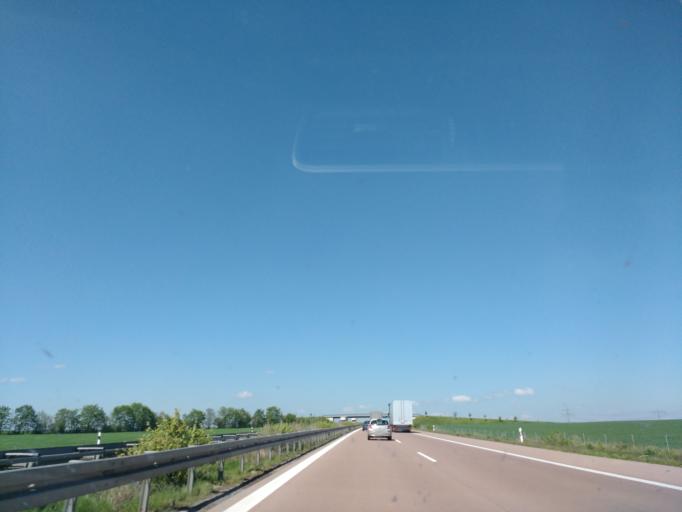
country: DE
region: Saxony-Anhalt
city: Obhausen
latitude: 51.4082
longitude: 11.6871
